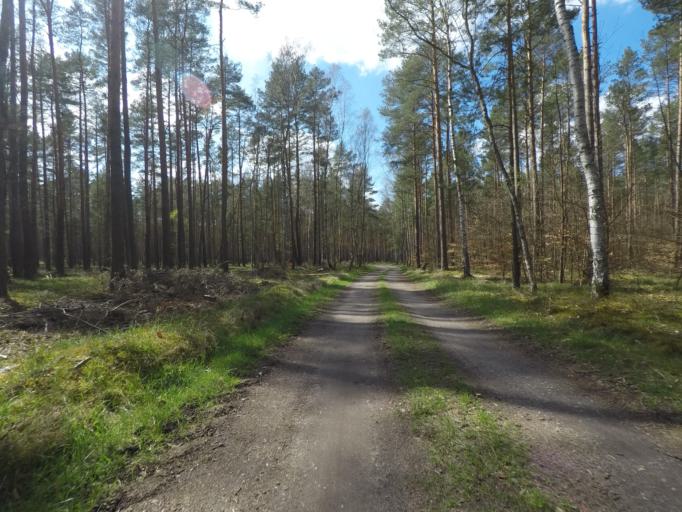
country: DE
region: Brandenburg
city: Melchow
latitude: 52.8210
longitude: 13.6797
